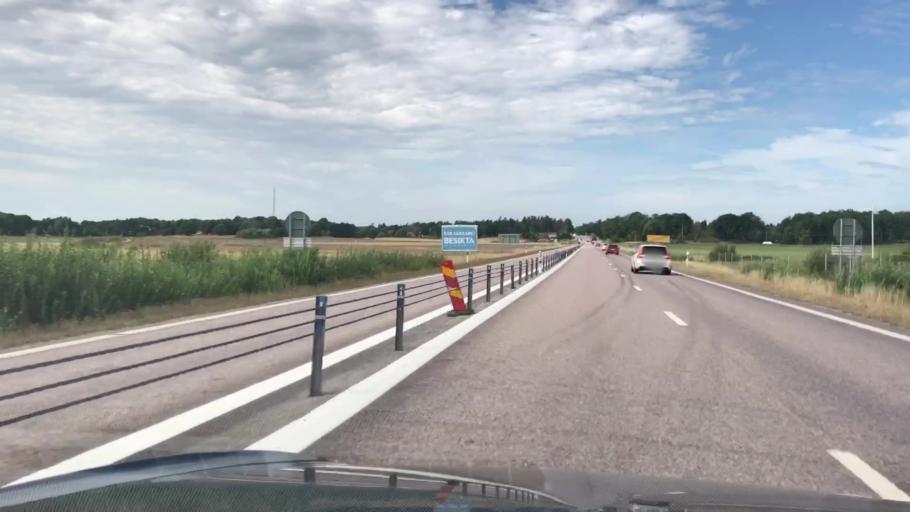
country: SE
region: Blekinge
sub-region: Ronneby Kommun
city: Kallinge
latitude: 56.2005
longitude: 15.3691
